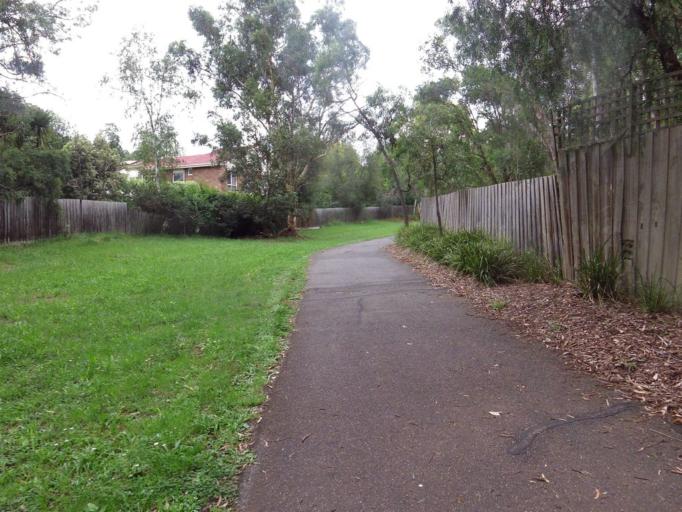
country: AU
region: Victoria
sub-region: Manningham
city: Donvale
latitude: -37.7748
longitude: 145.1851
